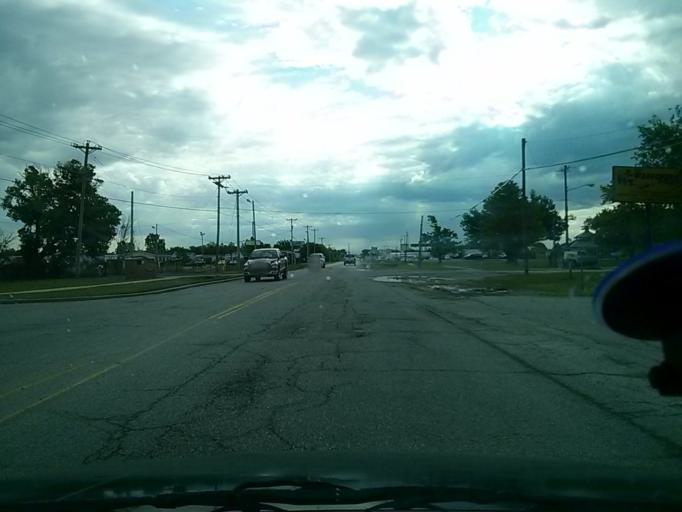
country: US
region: Oklahoma
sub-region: Rogers County
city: Catoosa
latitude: 36.1606
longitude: -95.8486
